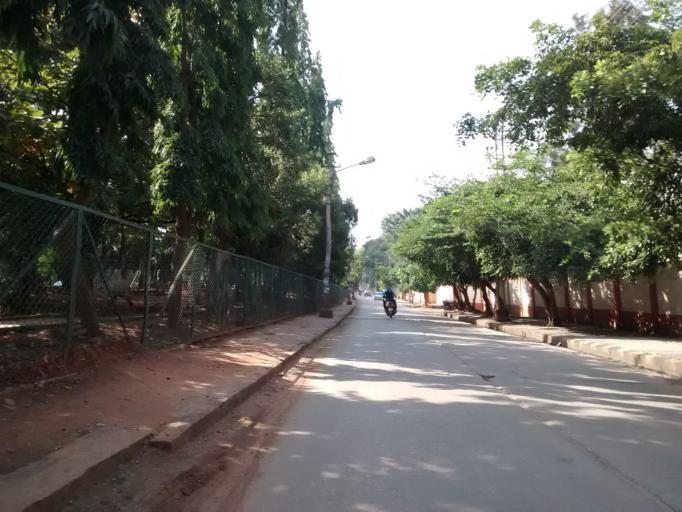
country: IN
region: Karnataka
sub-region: Bangalore Urban
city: Bangalore
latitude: 12.9635
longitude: 77.6642
